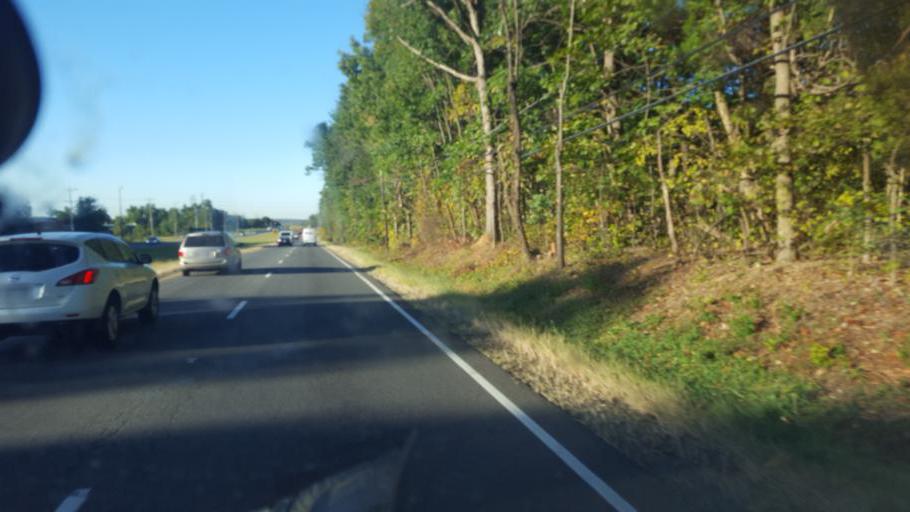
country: US
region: Virginia
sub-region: Fairfax County
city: Centreville
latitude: 38.8233
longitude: -77.4399
